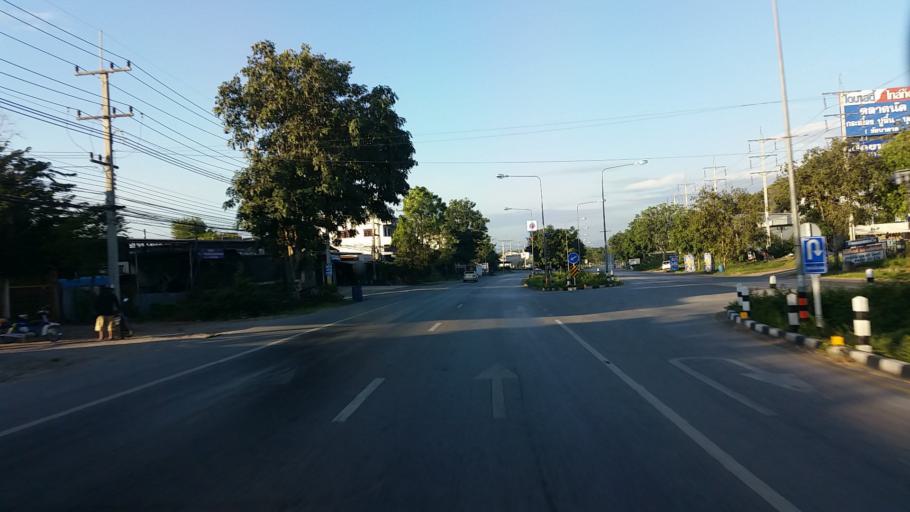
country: TH
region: Lop Buri
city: Chai Badan
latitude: 15.2123
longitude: 101.1227
